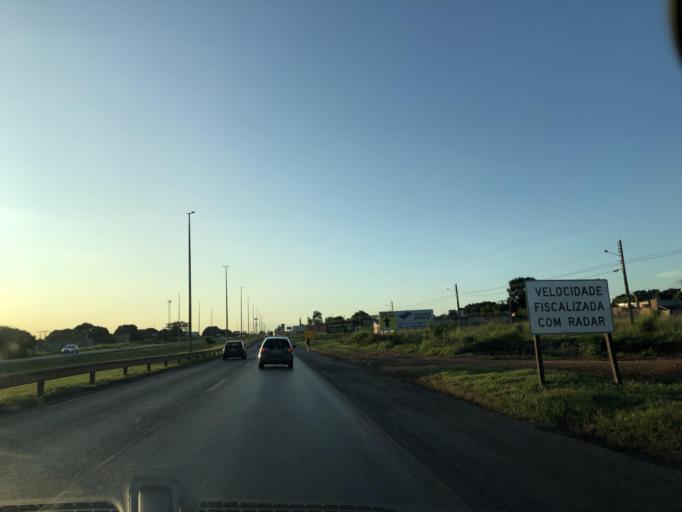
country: BR
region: Goias
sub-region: Luziania
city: Luziania
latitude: -16.1537
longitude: -47.9370
